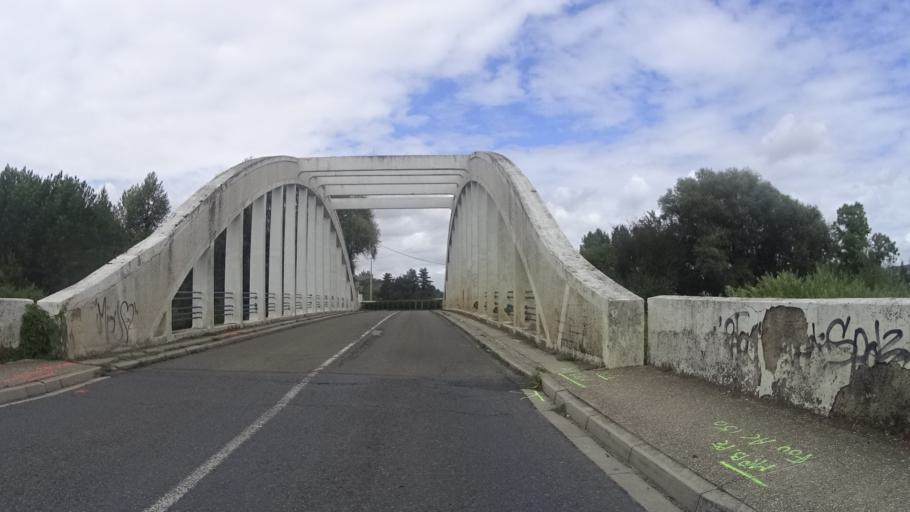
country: FR
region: Picardie
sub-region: Departement de l'Oise
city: Noyon
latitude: 49.5598
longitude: 2.9939
